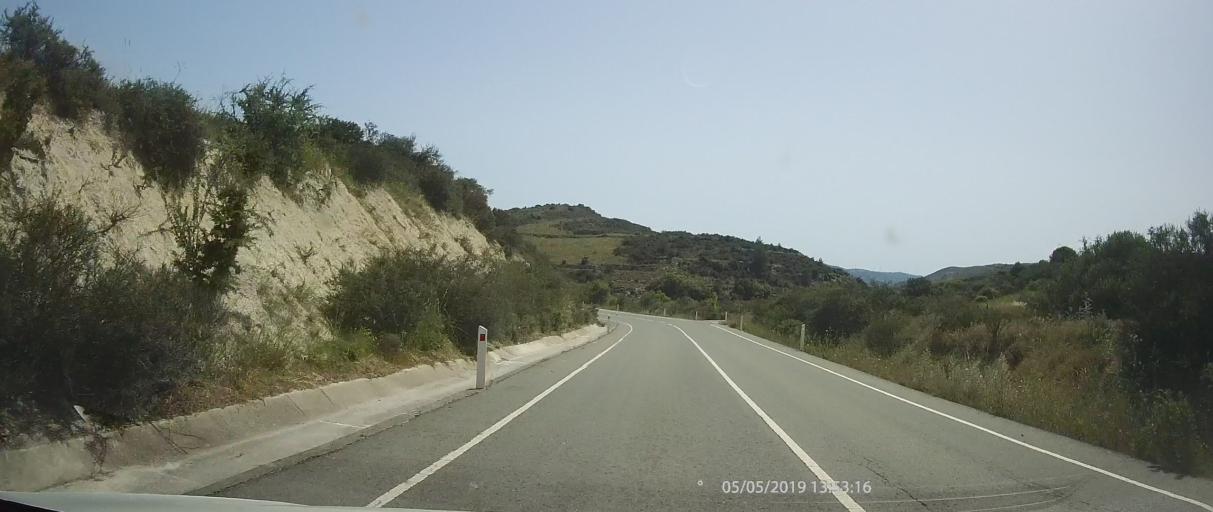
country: CY
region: Limassol
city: Pachna
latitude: 34.8230
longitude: 32.7247
